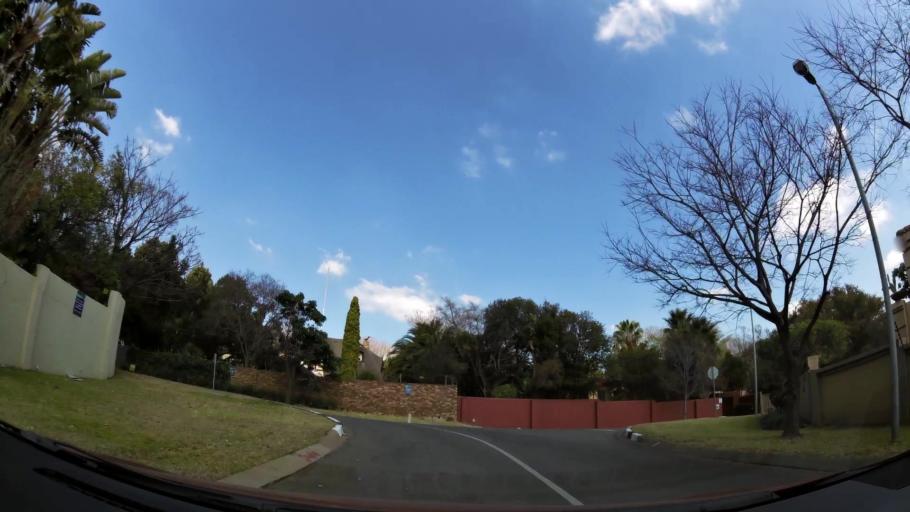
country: ZA
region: Gauteng
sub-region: City of Johannesburg Metropolitan Municipality
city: Roodepoort
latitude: -26.0821
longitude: 27.9537
